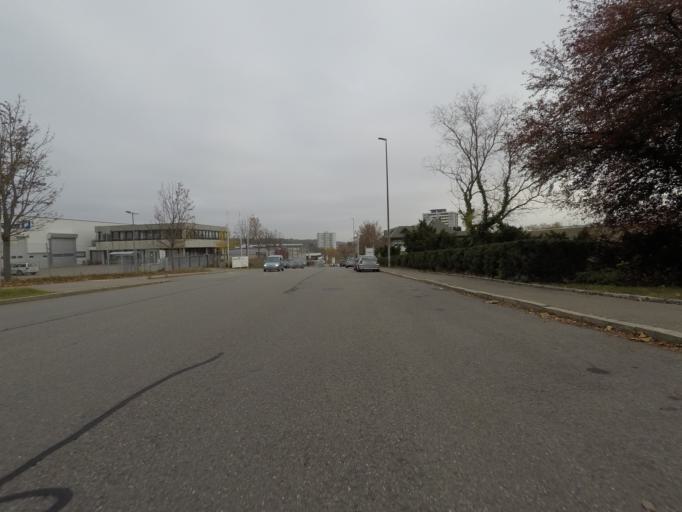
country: DE
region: Baden-Wuerttemberg
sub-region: Tuebingen Region
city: Reutlingen
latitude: 48.5115
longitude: 9.2291
